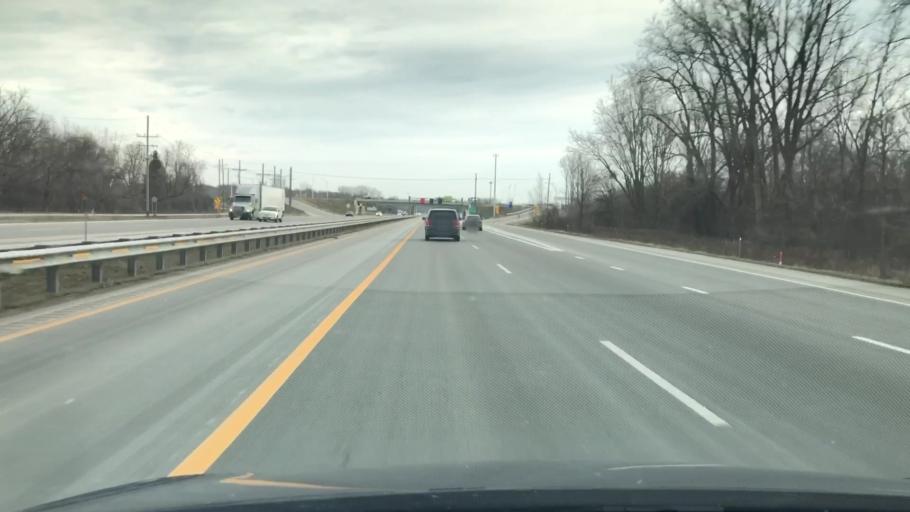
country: US
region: Michigan
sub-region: Livingston County
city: Whitmore Lake
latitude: 42.3828
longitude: -83.7591
